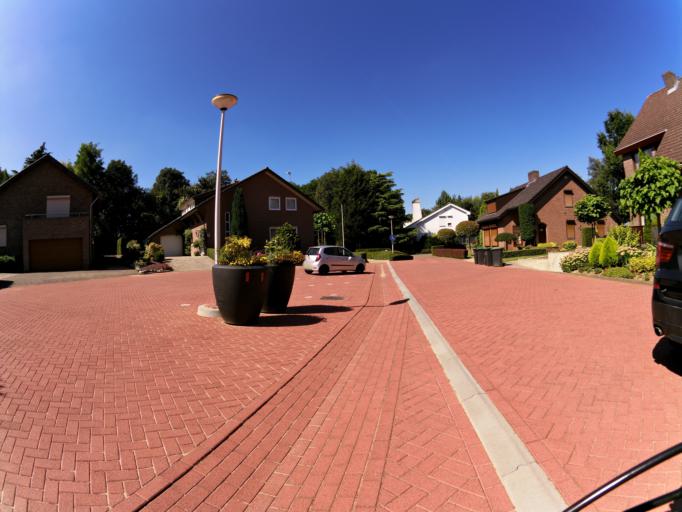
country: NL
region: Limburg
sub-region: Gemeente Kerkrade
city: Kerkrade
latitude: 50.8833
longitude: 6.0697
